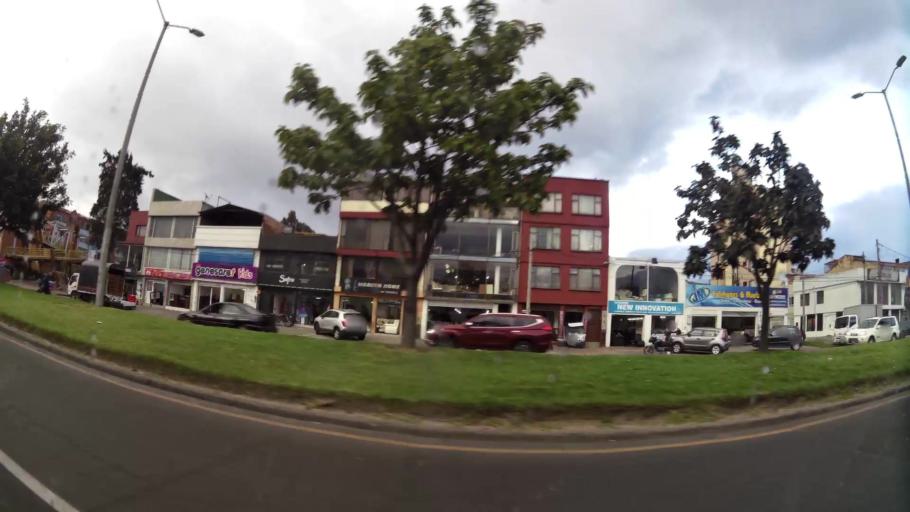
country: CO
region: Bogota D.C.
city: Bogota
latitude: 4.5996
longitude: -74.1171
